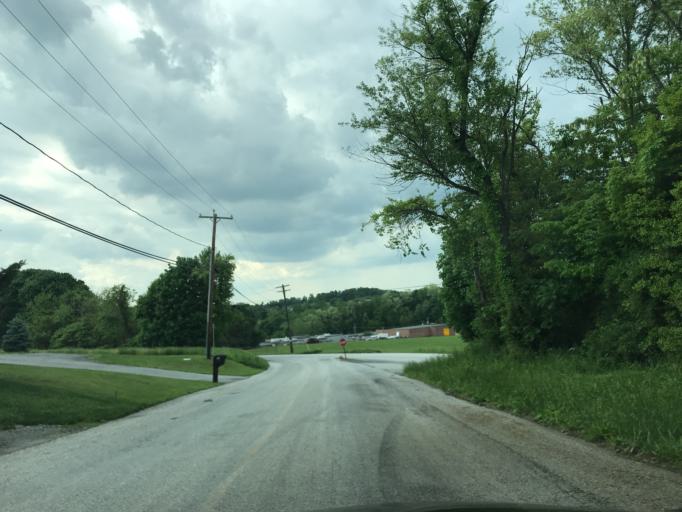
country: US
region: Pennsylvania
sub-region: York County
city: Susquehanna Trails
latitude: 39.7314
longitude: -76.3139
